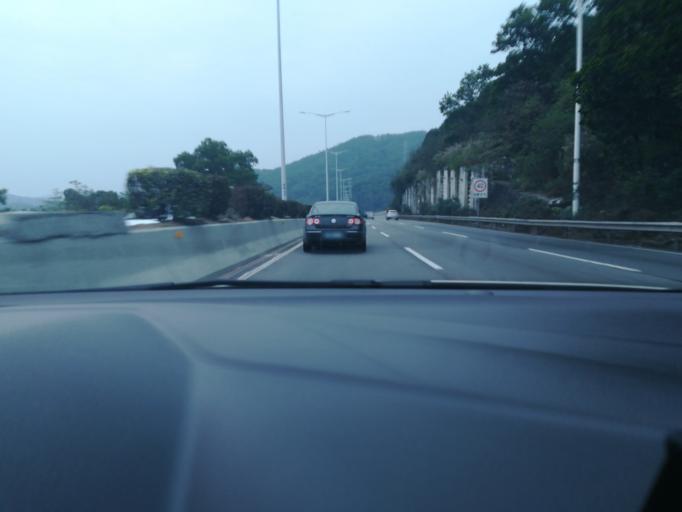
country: CN
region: Guangdong
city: Longdong
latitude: 23.2431
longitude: 113.3524
